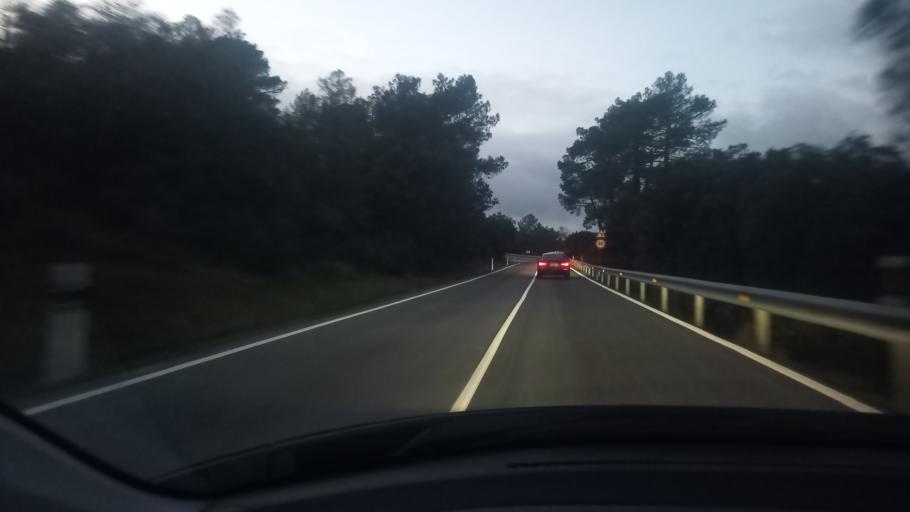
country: ES
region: Madrid
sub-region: Provincia de Madrid
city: Robledo de Chavela
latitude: 40.4615
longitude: -4.2617
